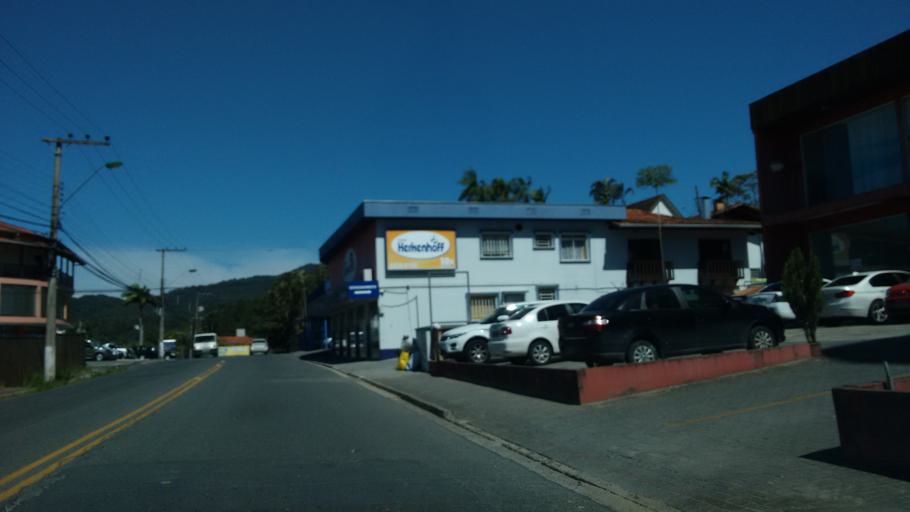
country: BR
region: Santa Catarina
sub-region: Blumenau
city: Blumenau
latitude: -26.9165
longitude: -49.1084
